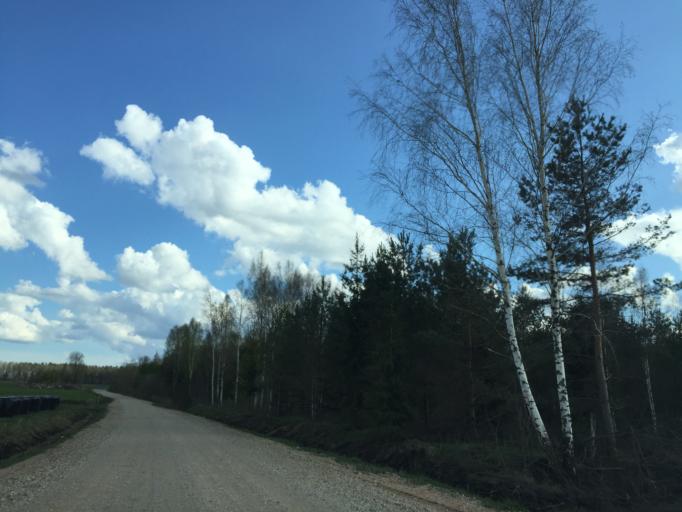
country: LV
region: Beverina
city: Murmuiza
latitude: 57.4337
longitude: 25.5447
